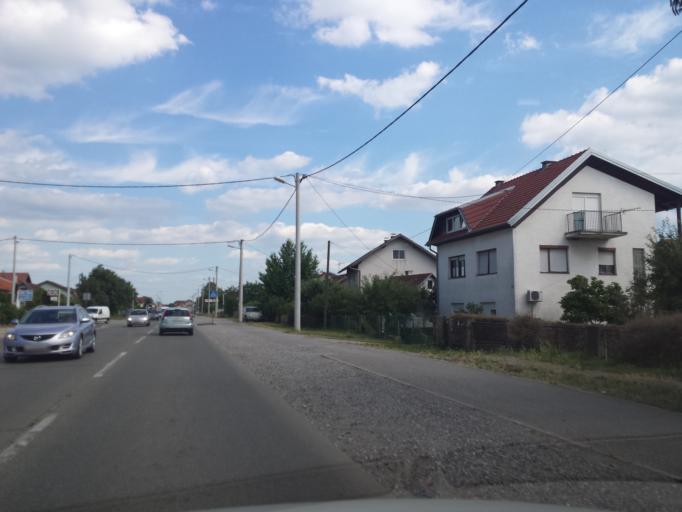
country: HR
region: Grad Zagreb
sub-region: Sesvete
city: Sesvete
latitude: 45.8198
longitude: 16.1655
